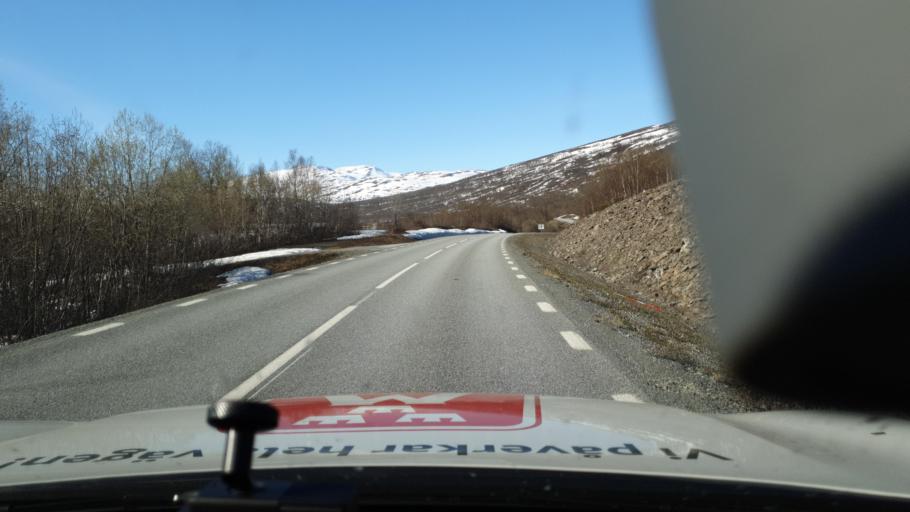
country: NO
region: Nordland
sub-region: Rana
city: Mo i Rana
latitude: 66.0628
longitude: 14.8723
